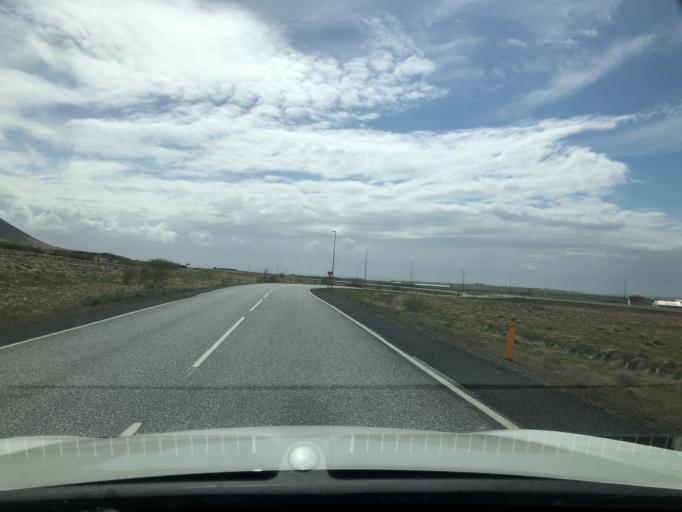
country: IS
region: Capital Region
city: Reykjavik
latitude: 64.2767
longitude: -21.8357
